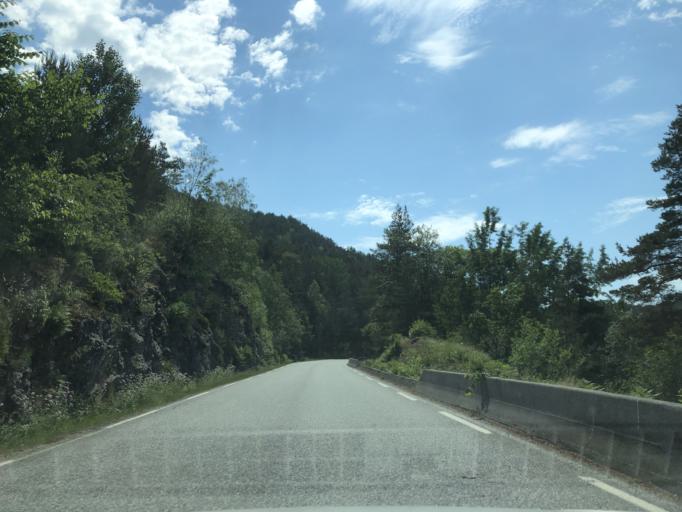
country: NO
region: Hordaland
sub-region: Jondal
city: Jondal
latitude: 60.2982
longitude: 6.2433
